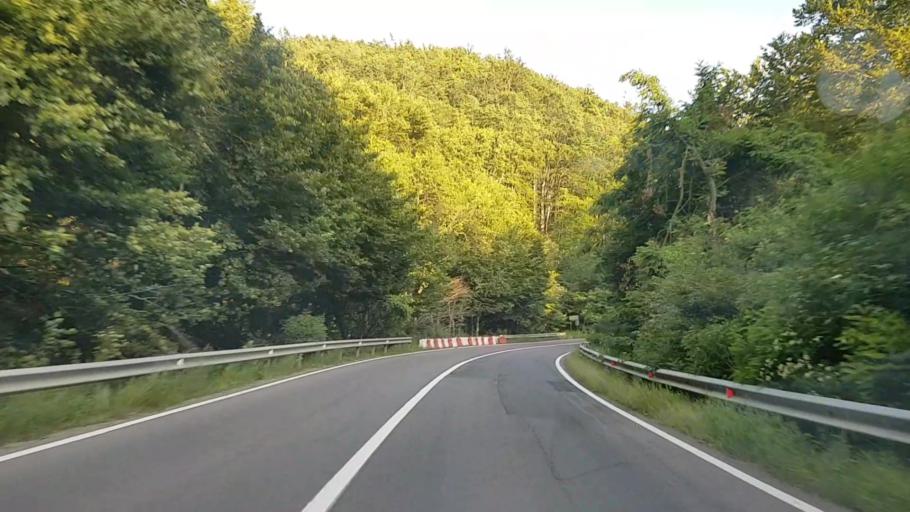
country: RO
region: Harghita
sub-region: Comuna Corund
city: Corund
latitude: 46.4471
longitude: 25.2277
